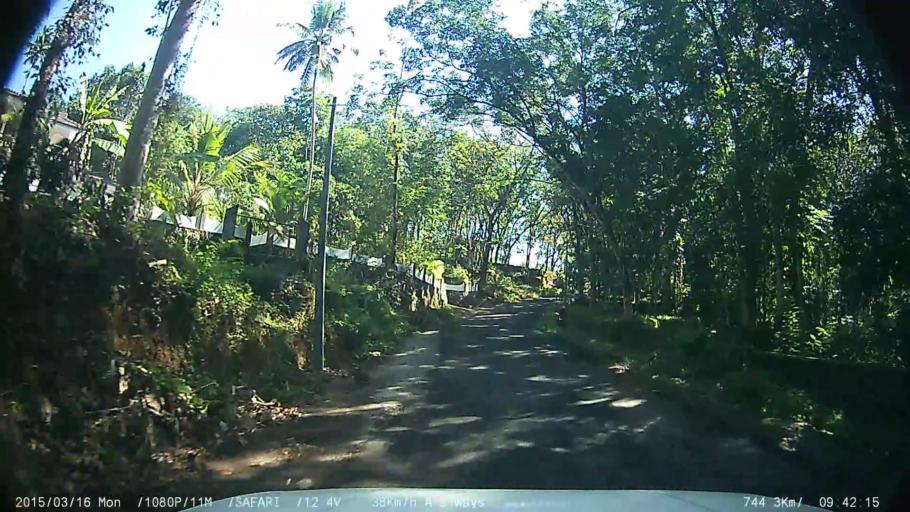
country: IN
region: Kerala
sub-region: Kottayam
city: Palackattumala
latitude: 9.7861
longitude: 76.6020
